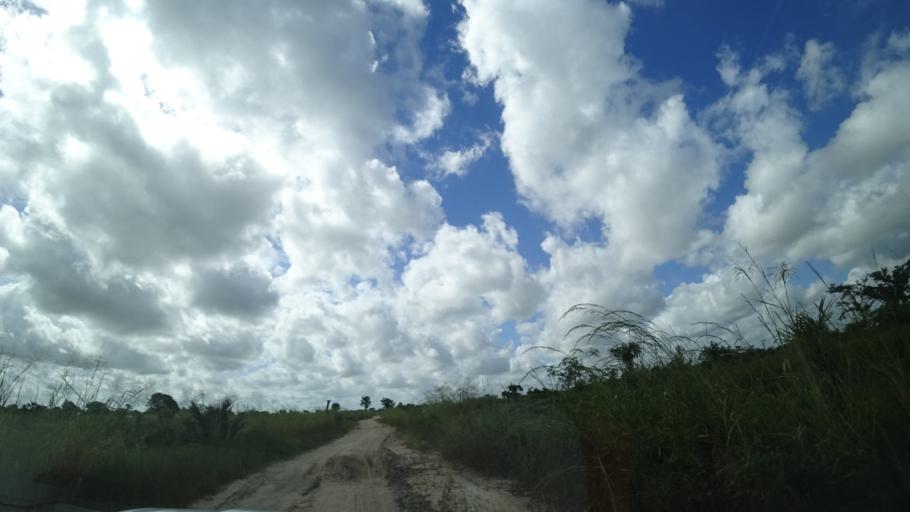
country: MZ
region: Sofala
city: Dondo
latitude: -19.3872
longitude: 34.5872
